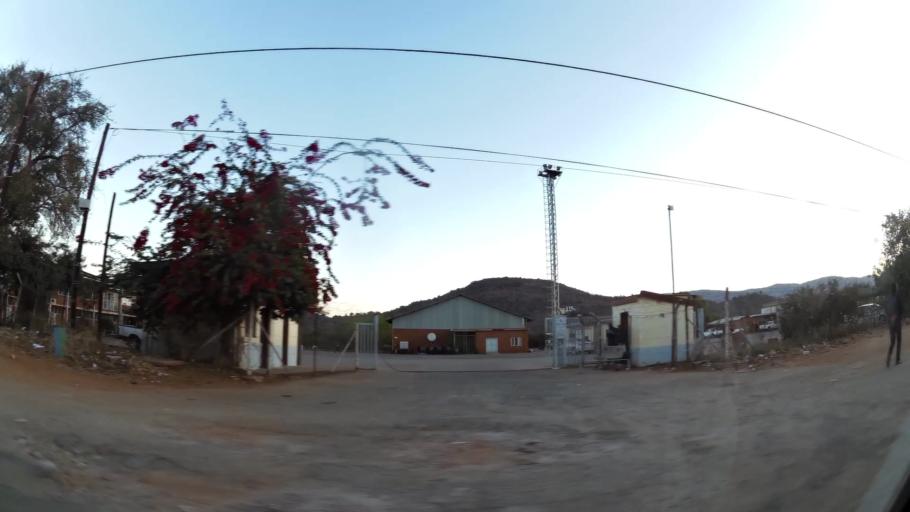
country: ZA
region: Limpopo
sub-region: Waterberg District Municipality
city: Mokopane
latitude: -24.1434
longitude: 28.9732
